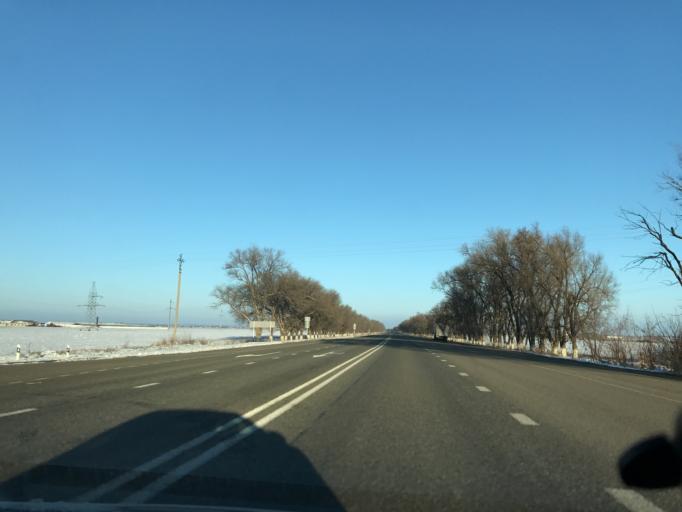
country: RU
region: Stavropol'skiy
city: Bezopasnoye
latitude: 45.6180
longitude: 41.9396
